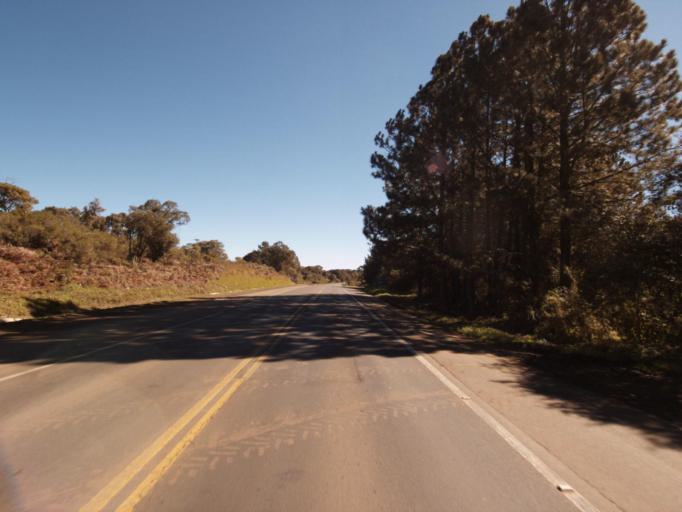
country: BR
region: Santa Catarina
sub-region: Xanxere
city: Xanxere
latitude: -26.8785
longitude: -52.1870
